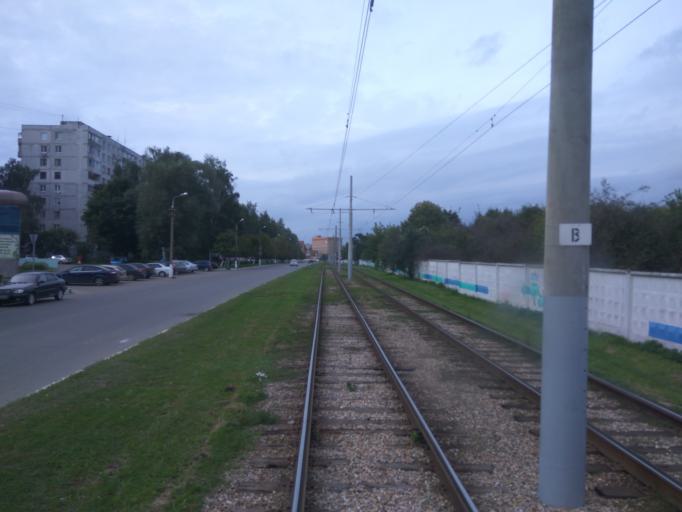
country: RU
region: Moskovskaya
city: Kolomna
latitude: 55.0616
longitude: 38.7575
